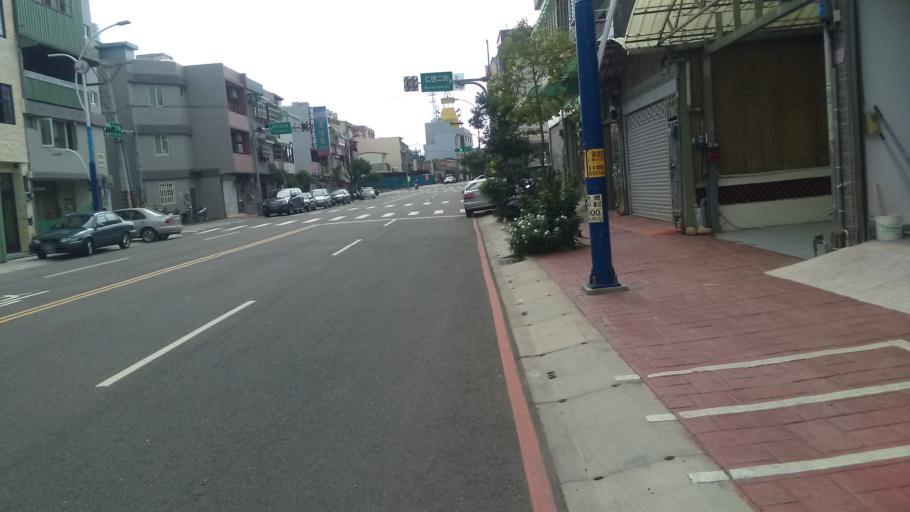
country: TW
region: Taiwan
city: Taoyuan City
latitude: 24.9514
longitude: 121.2626
